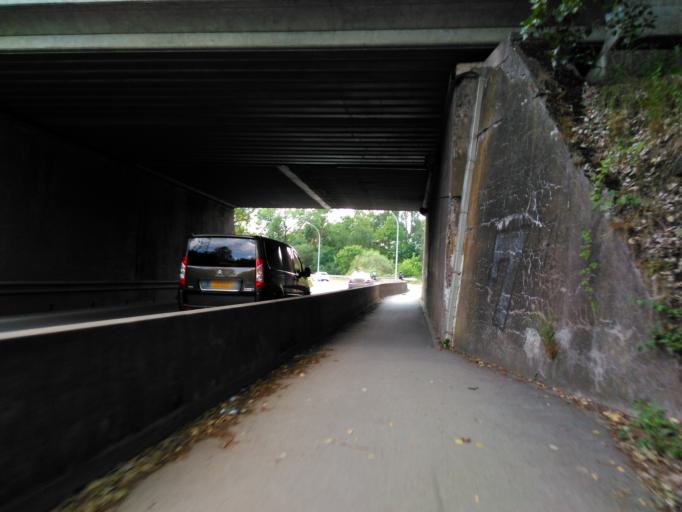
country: LU
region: Luxembourg
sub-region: Canton d'Esch-sur-Alzette
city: Schifflange
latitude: 49.5088
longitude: 6.0002
